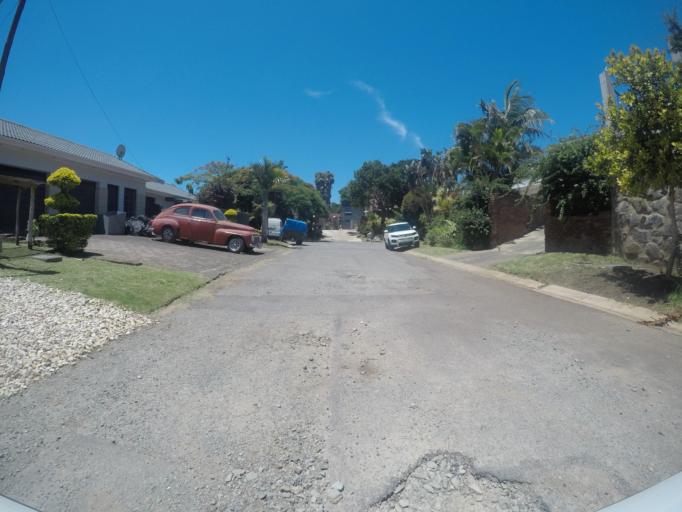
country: ZA
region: Eastern Cape
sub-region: Buffalo City Metropolitan Municipality
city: East London
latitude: -32.9327
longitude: 28.0096
